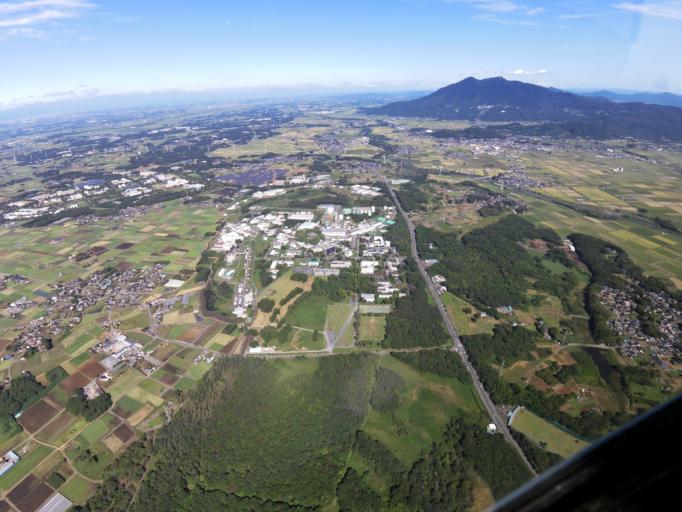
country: JP
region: Ibaraki
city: Tsukuba
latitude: 36.1380
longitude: 140.0768
